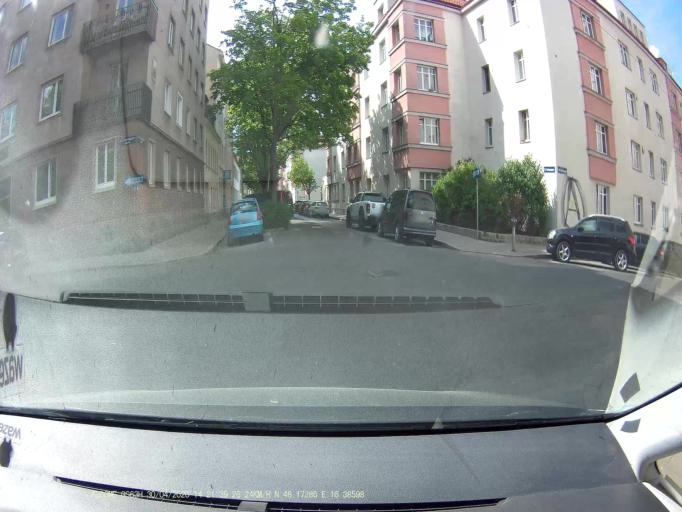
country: AT
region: Vienna
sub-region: Wien Stadt
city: Vienna
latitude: 48.1729
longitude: 16.3857
